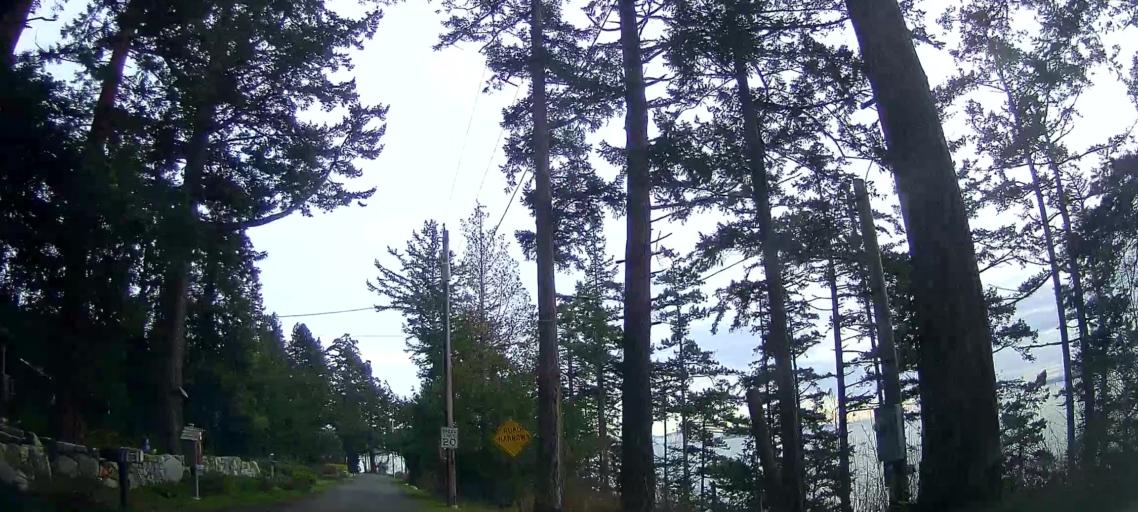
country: US
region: Washington
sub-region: Skagit County
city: Anacortes
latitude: 48.5765
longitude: -122.5526
